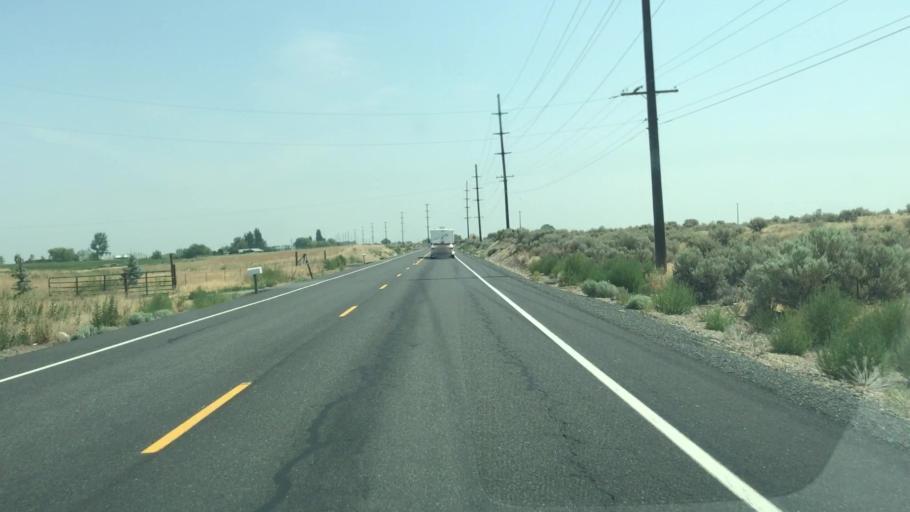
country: US
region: Washington
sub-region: Grant County
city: Quincy
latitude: 47.1601
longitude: -119.8903
